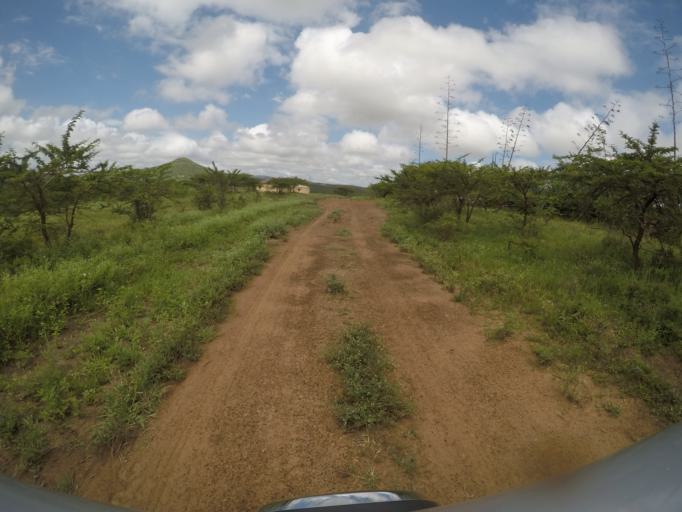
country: ZA
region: KwaZulu-Natal
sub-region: uThungulu District Municipality
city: Empangeni
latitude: -28.5833
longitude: 31.8532
